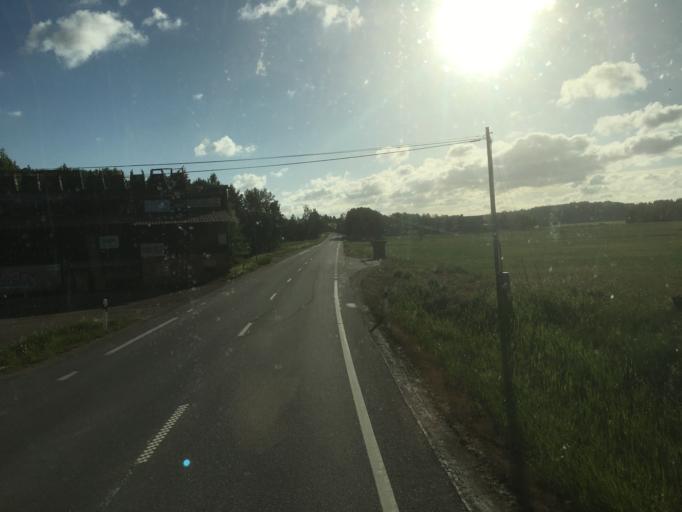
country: SE
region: Gaevleborg
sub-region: Sandvikens Kommun
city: Jarbo
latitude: 60.5696
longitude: 16.4927
